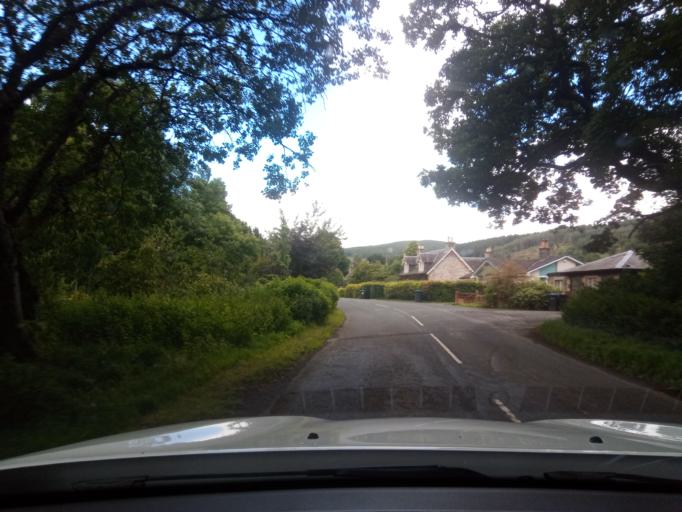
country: GB
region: Scotland
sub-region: The Scottish Borders
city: Selkirk
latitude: 55.5598
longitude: -2.9374
